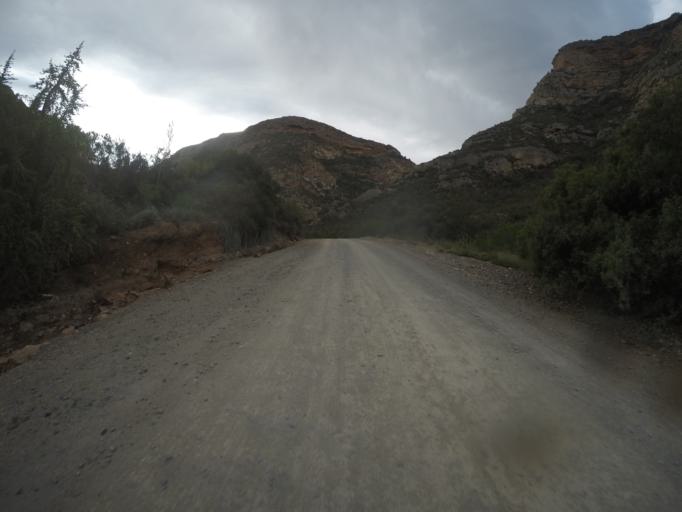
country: ZA
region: Eastern Cape
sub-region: Cacadu District Municipality
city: Willowmore
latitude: -33.5135
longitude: 23.8198
